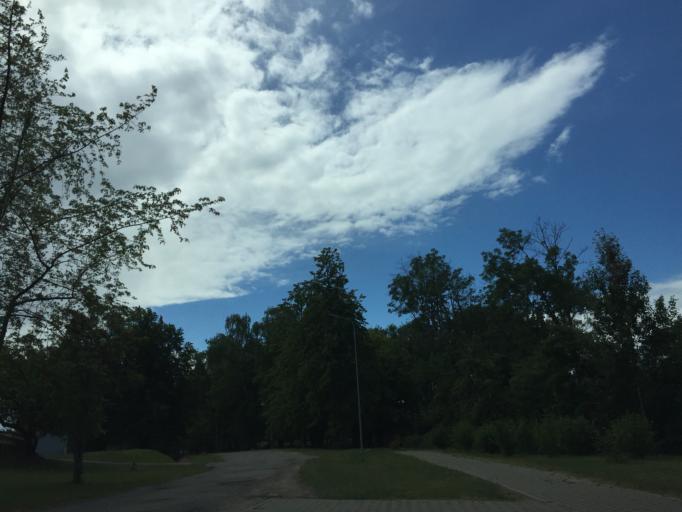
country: LV
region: Saulkrastu
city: Saulkrasti
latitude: 57.3188
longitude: 24.4171
